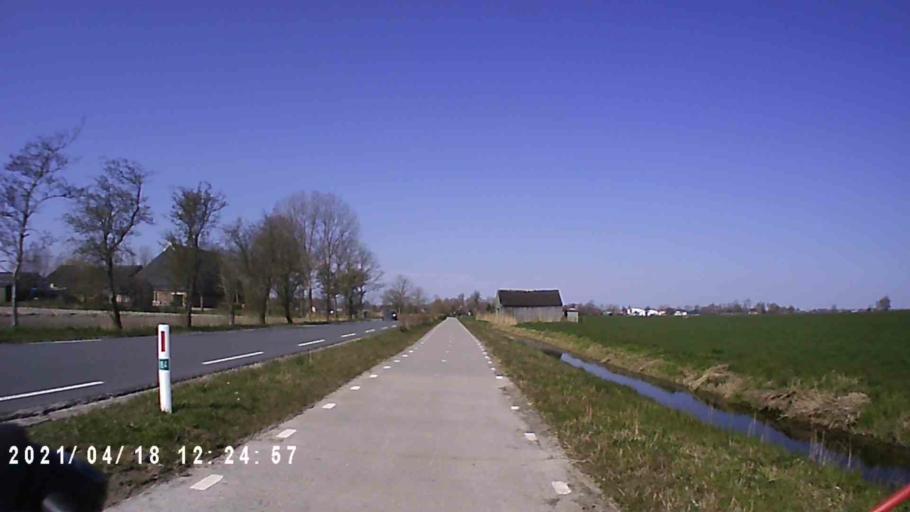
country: NL
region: Friesland
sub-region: Gemeente Dongeradeel
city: Anjum
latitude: 53.3279
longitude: 6.1143
